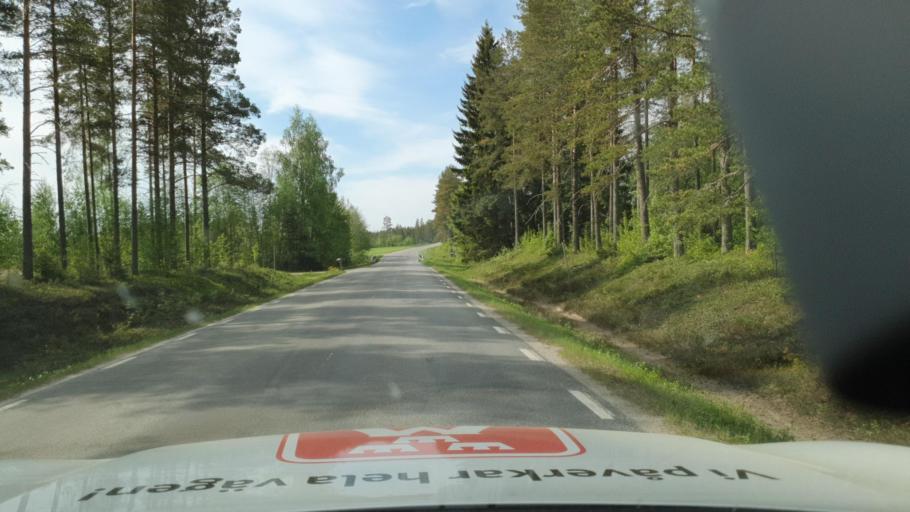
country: SE
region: Vaesterbotten
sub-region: Umea Kommun
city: Roback
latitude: 63.7566
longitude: 20.2072
